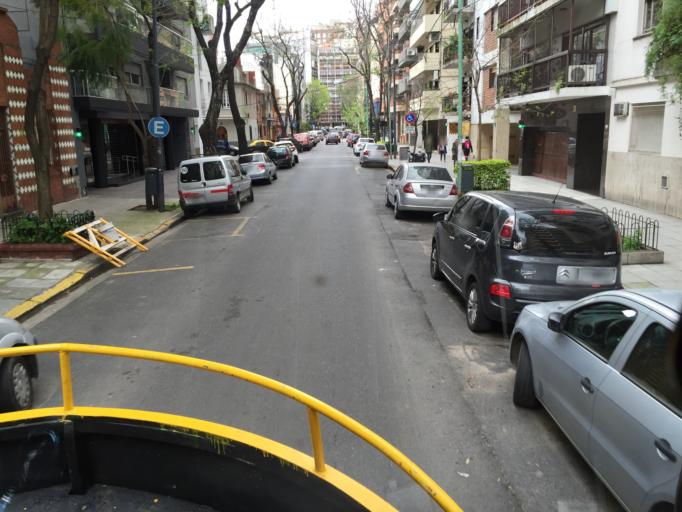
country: AR
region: Buenos Aires F.D.
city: Colegiales
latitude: -34.5682
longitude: -58.4356
